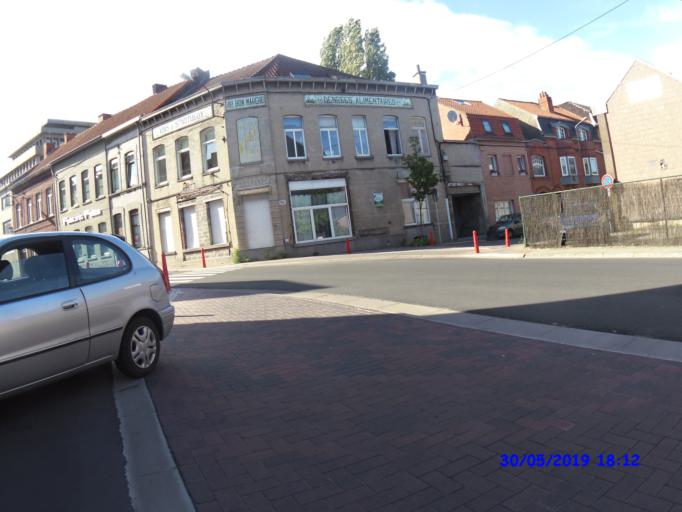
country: BE
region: Wallonia
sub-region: Province du Hainaut
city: Mouscron
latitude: 50.7426
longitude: 3.2272
